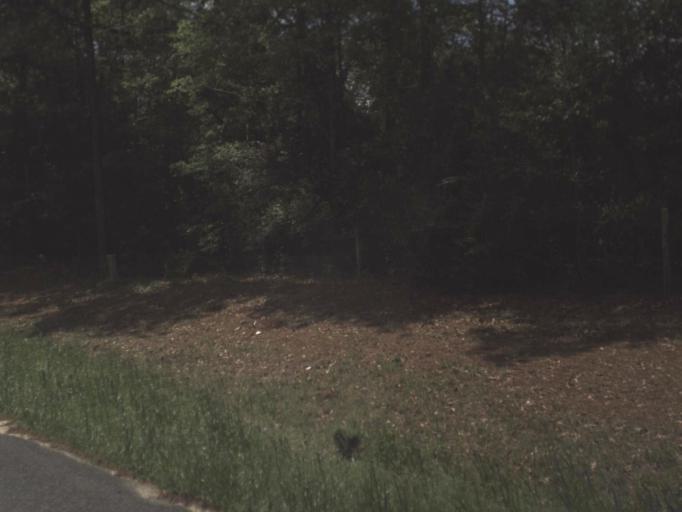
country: US
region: Florida
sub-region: Okaloosa County
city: Crestview
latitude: 30.9663
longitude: -86.6319
